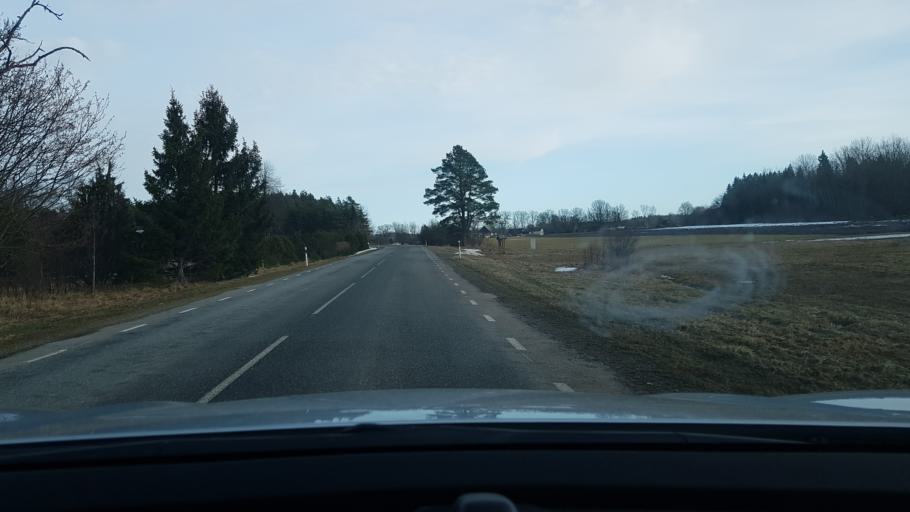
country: EE
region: Saare
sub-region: Kuressaare linn
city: Kuressaare
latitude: 58.4045
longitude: 22.6450
